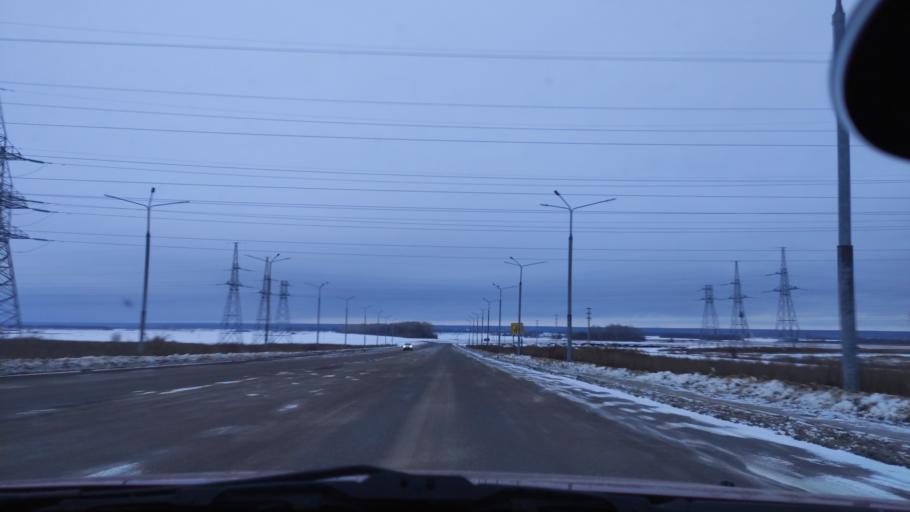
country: RU
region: Tambov
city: Donskoye
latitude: 52.7875
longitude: 41.4306
